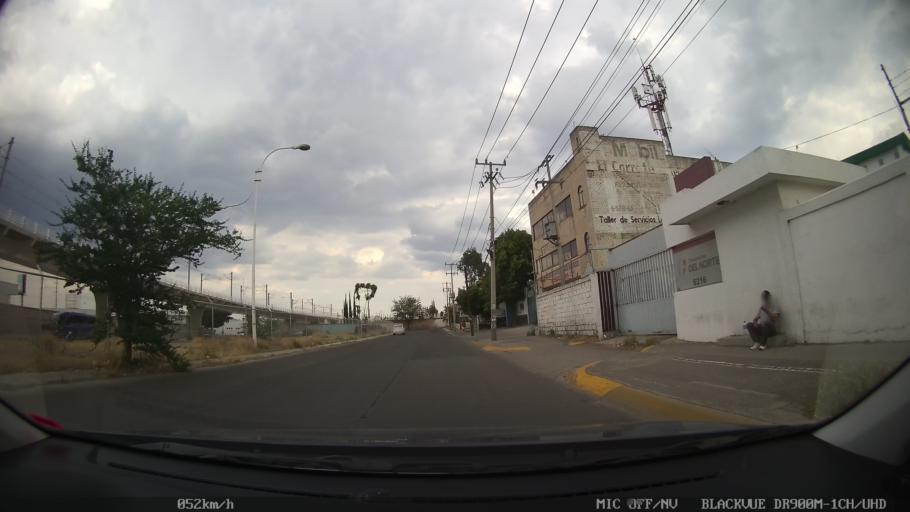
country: MX
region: Jalisco
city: Tlaquepaque
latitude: 20.6224
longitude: -103.2835
